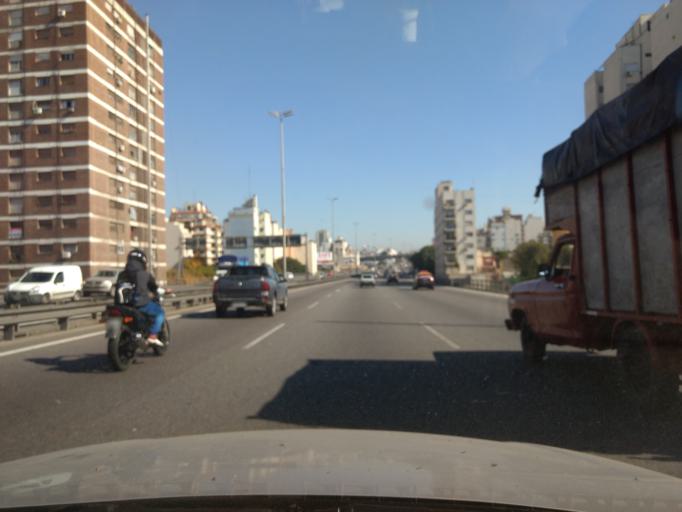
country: AR
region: Buenos Aires F.D.
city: Buenos Aires
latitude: -34.6227
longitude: -58.3735
